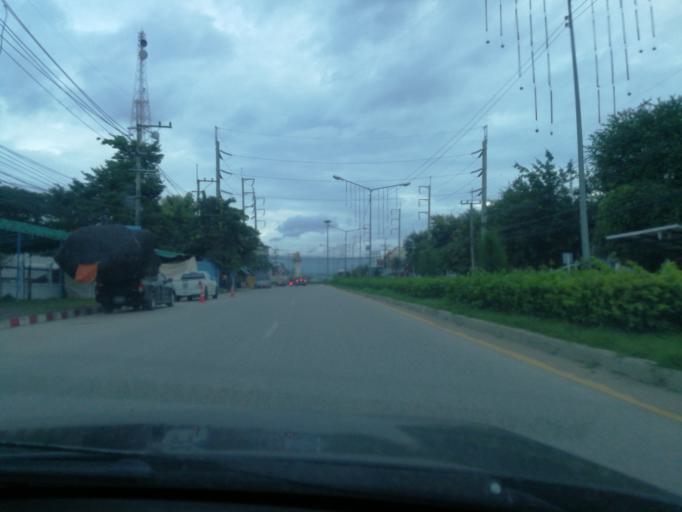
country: TH
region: Chiang Mai
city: Hot
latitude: 18.1922
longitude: 98.6120
